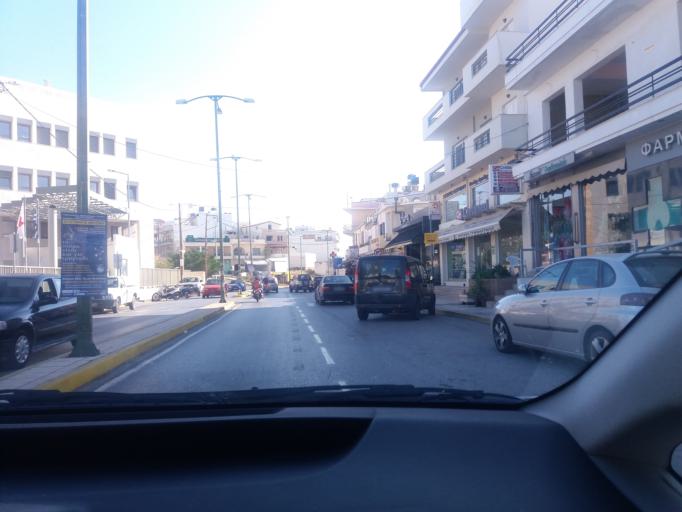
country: GR
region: Crete
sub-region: Nomos Lasithiou
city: Agios Nikolaos
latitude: 35.1949
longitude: 25.7129
